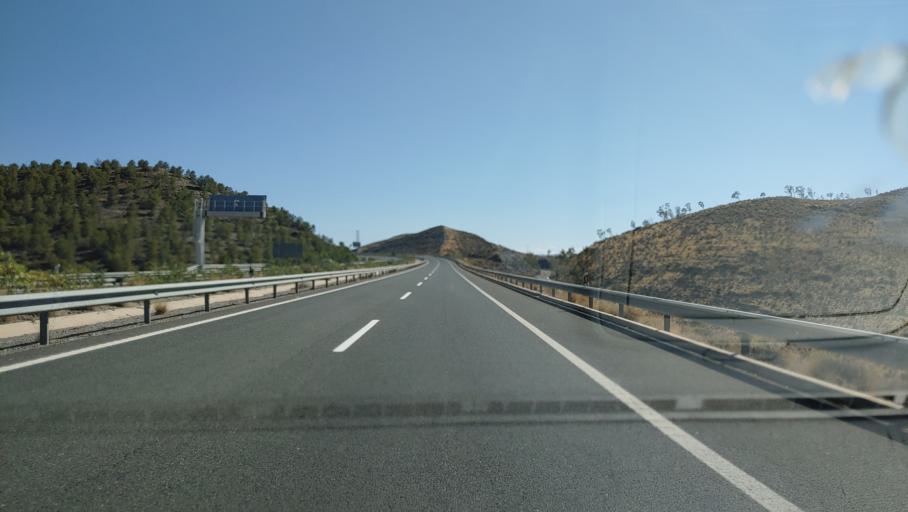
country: ES
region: Andalusia
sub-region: Provincia de Almeria
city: Gergal
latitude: 37.1012
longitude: -2.5296
